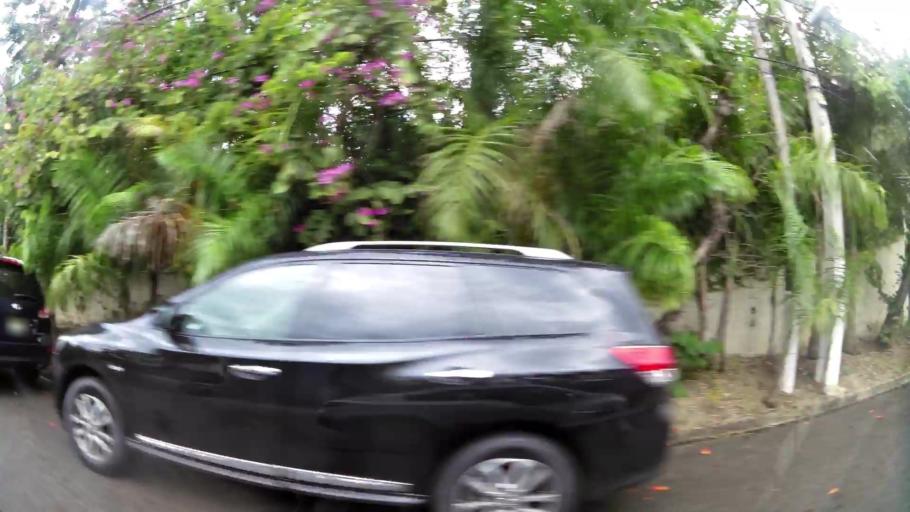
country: DO
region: Nacional
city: La Agustina
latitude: 18.5115
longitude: -69.9523
